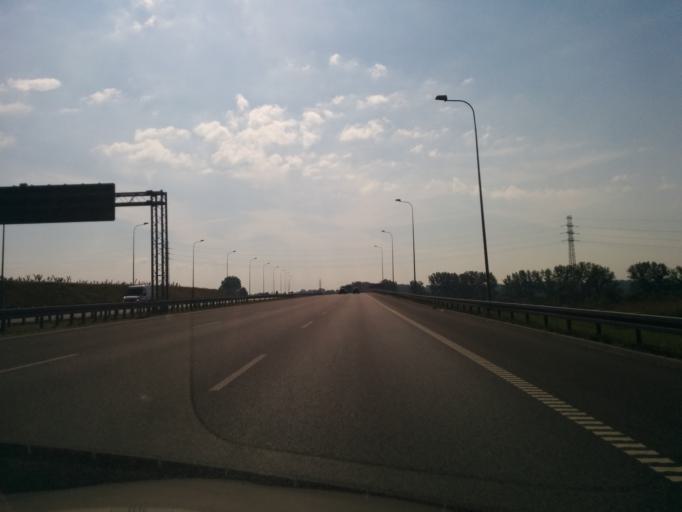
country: PL
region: Silesian Voivodeship
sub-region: Piekary Slaskie
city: Piekary Slaskie
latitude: 50.3713
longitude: 18.9059
